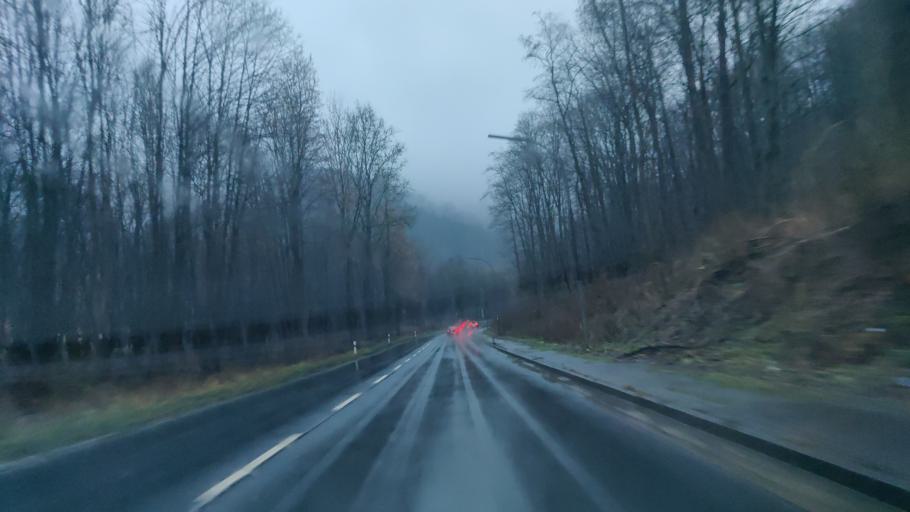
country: DE
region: Lower Saxony
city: Bad Lauterberg im Harz
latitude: 51.6374
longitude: 10.4866
